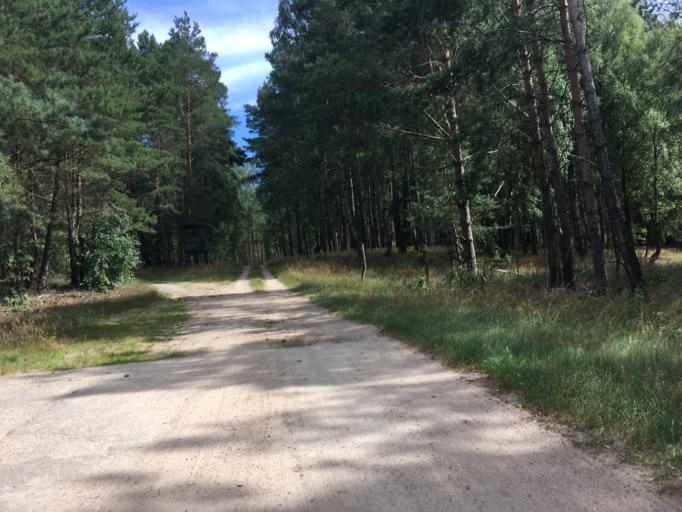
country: DE
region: Brandenburg
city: Rheinsberg
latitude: 53.0378
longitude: 12.9098
